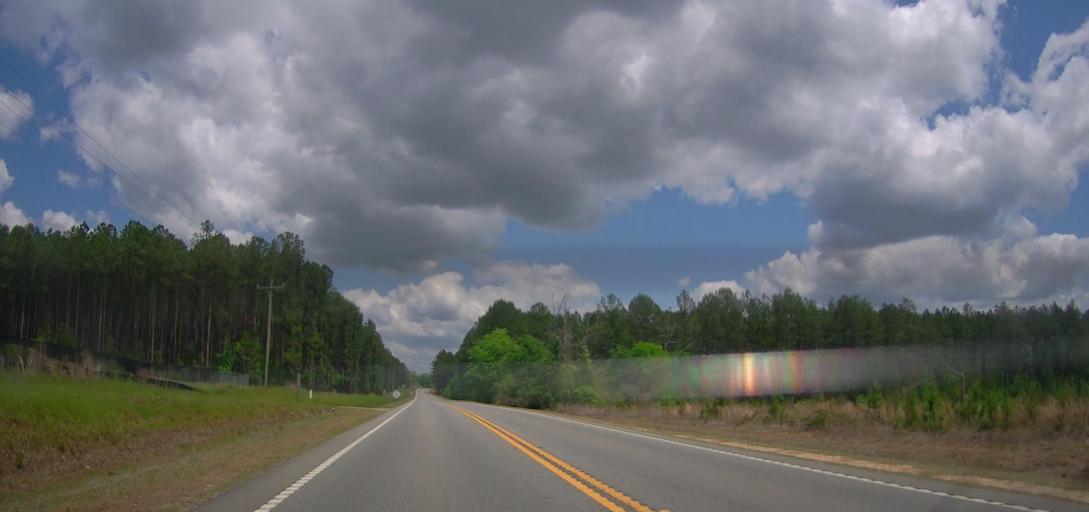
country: US
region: Georgia
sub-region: Laurens County
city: East Dublin
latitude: 32.5648
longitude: -82.8086
